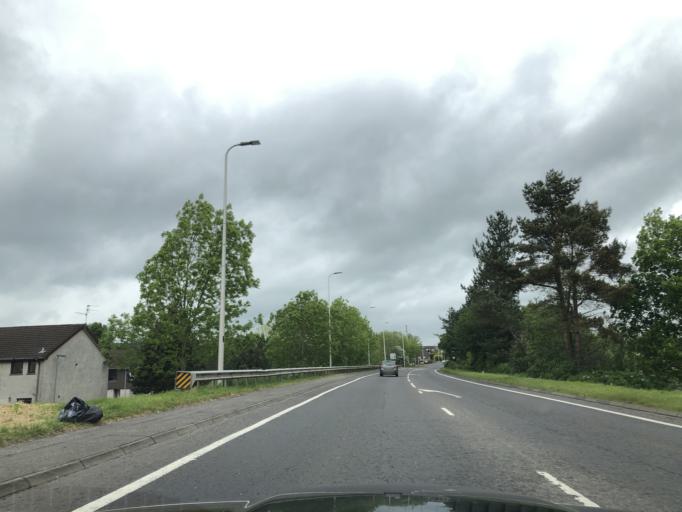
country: GB
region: Northern Ireland
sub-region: Lisburn District
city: Lisburn
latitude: 54.5228
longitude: -6.0737
